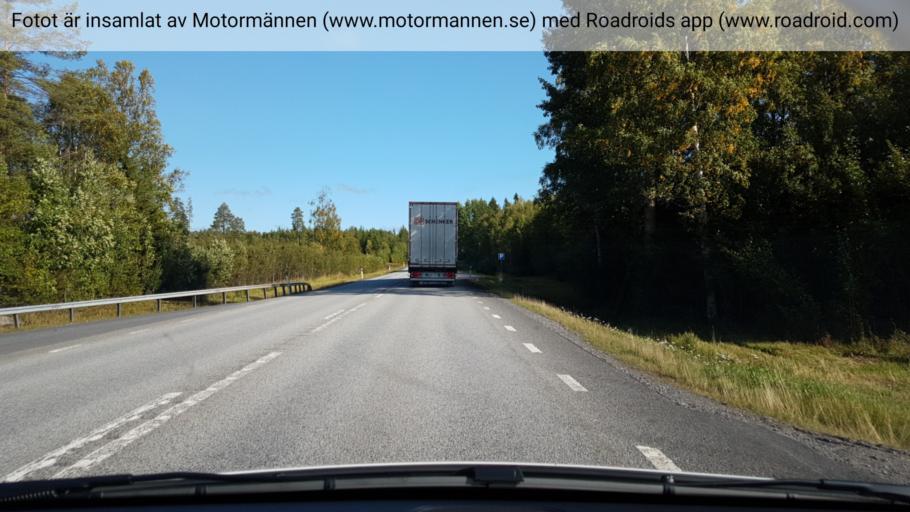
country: SE
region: Vaesterbotten
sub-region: Robertsfors Kommun
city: Robertsfors
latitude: 64.2465
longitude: 21.0351
